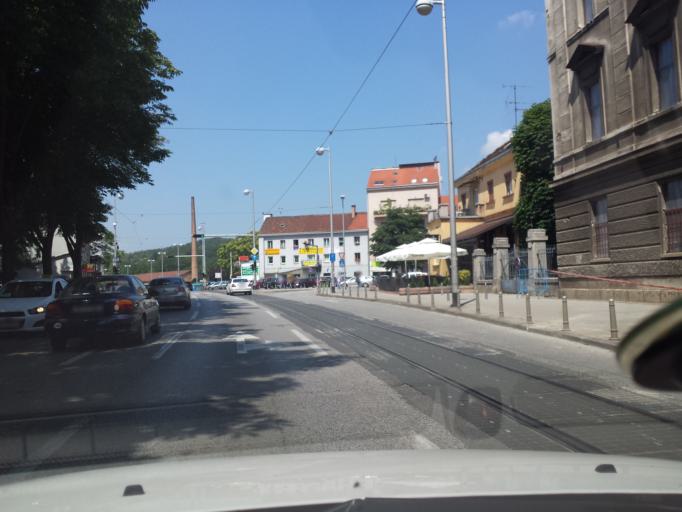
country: HR
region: Grad Zagreb
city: Zagreb - Centar
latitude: 45.8148
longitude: 15.9365
